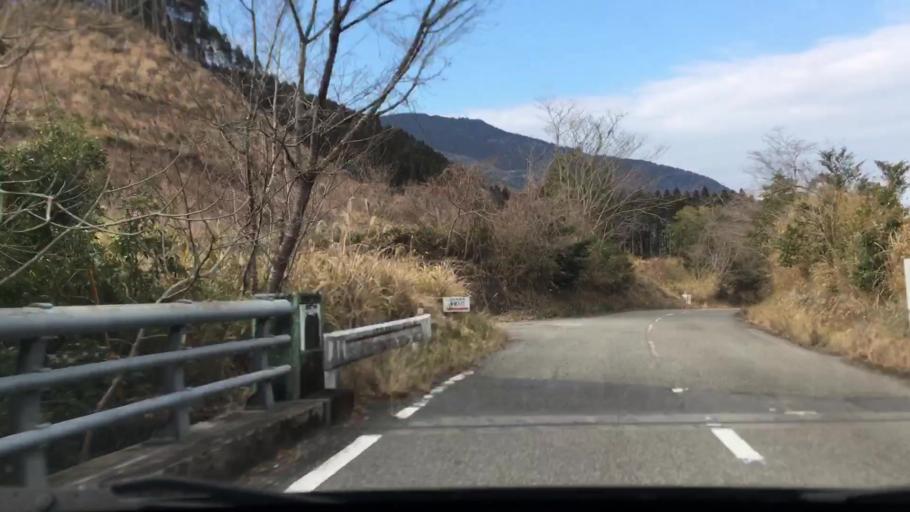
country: JP
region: Miyazaki
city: Nichinan
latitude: 31.7083
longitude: 131.3266
